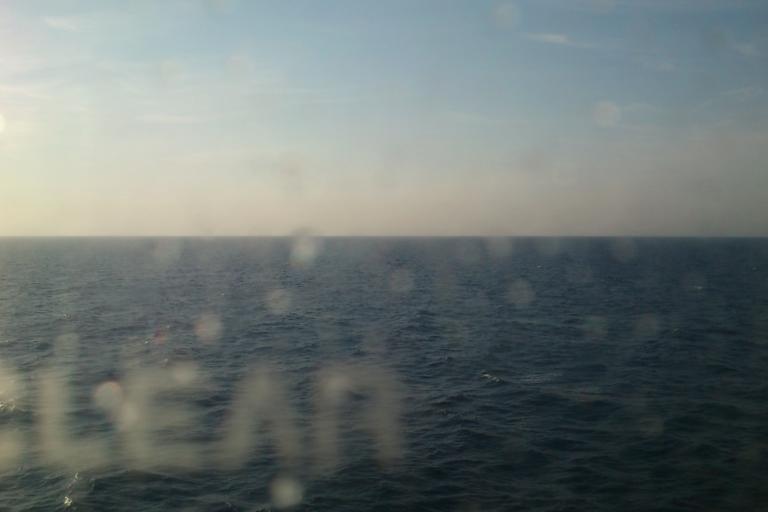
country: JP
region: Ishikawa
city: Nanao
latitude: 37.7929
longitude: 136.4340
